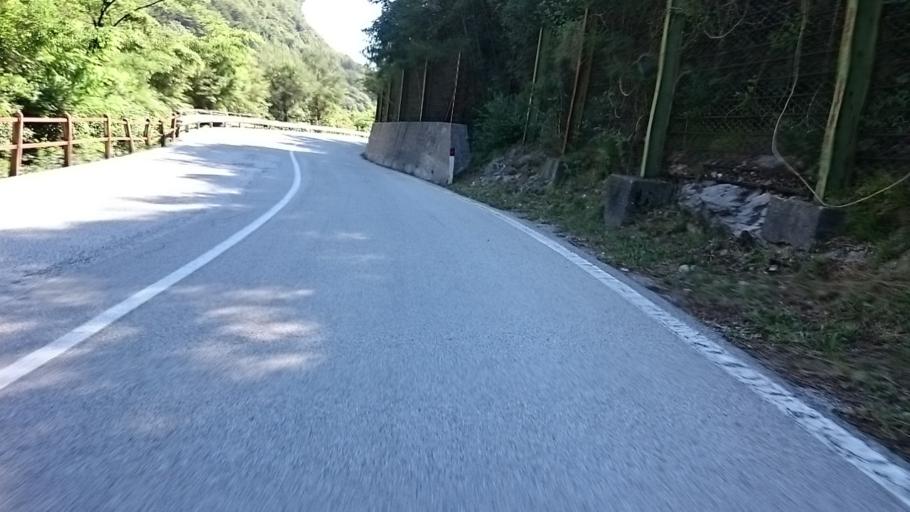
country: IT
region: Veneto
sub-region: Provincia di Belluno
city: Castello Lavazzo
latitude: 46.2985
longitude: 12.3142
